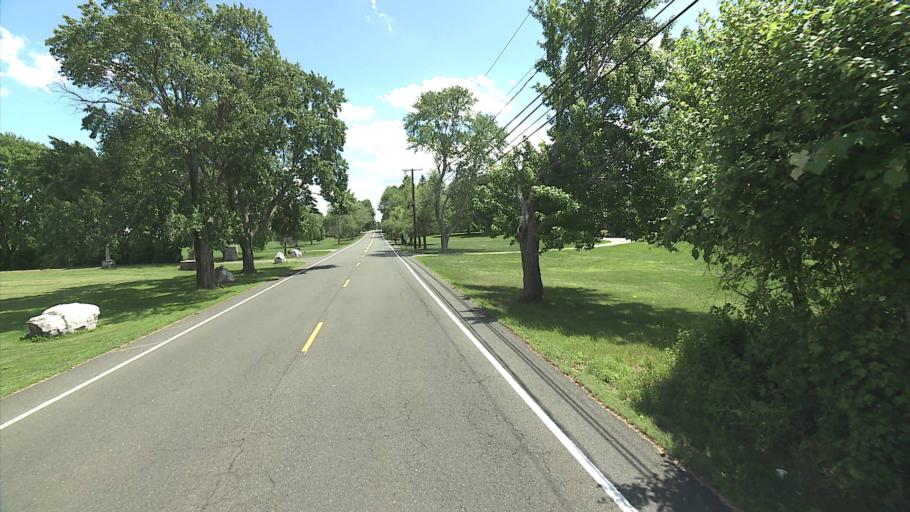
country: US
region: Massachusetts
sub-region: Hampden County
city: East Longmeadow
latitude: 42.0292
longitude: -72.4884
